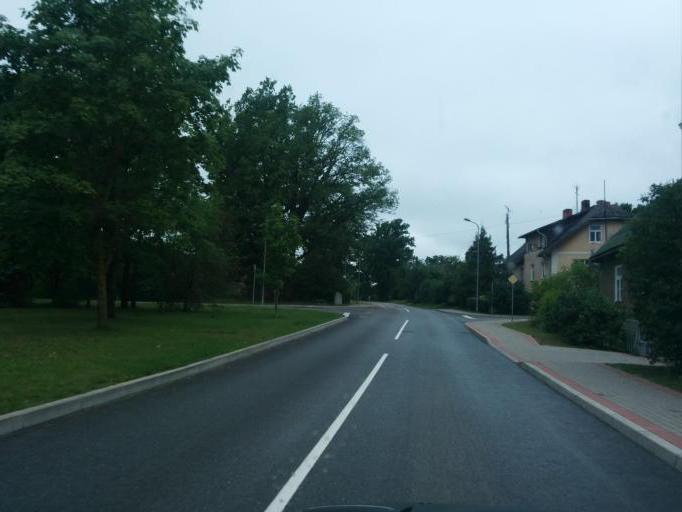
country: LV
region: Smiltene
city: Smiltene
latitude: 57.4255
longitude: 25.8946
